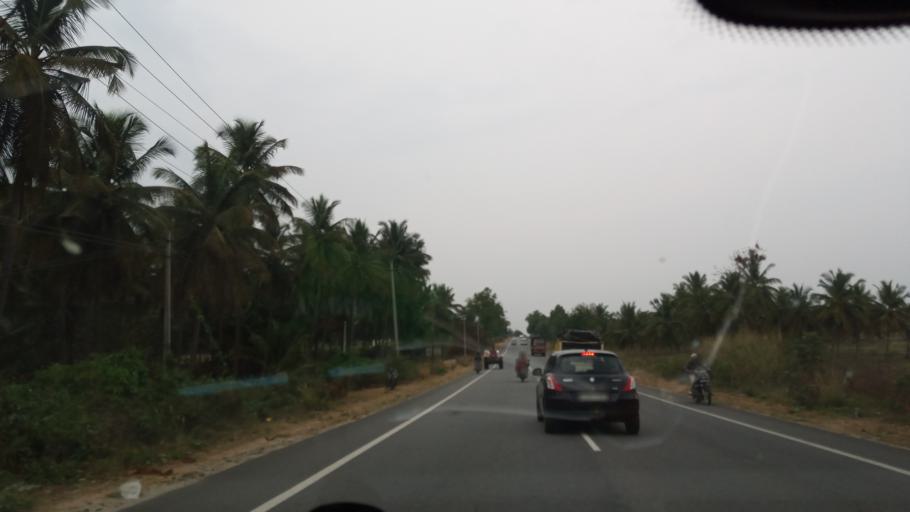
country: IN
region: Karnataka
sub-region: Mandya
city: Belluru
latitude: 12.9320
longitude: 76.7498
